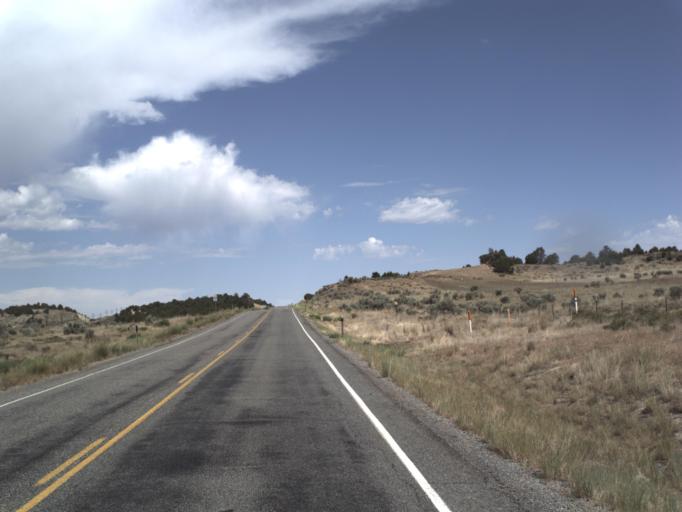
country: US
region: Utah
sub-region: Utah County
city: Genola
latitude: 39.9500
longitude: -112.2357
